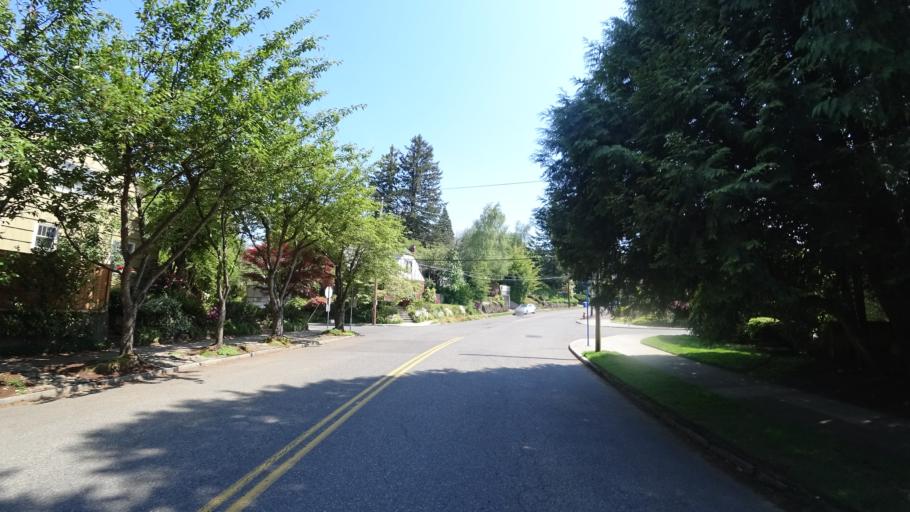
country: US
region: Oregon
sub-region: Multnomah County
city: Portland
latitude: 45.4963
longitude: -122.7021
